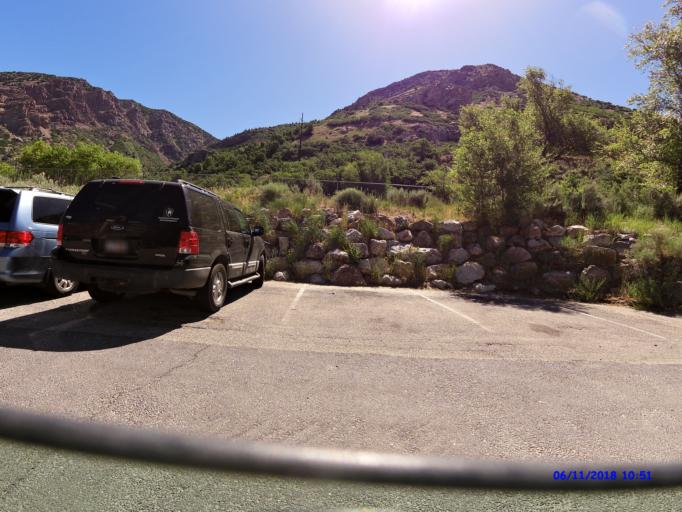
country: US
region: Utah
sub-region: Weber County
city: Ogden
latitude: 41.2108
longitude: -111.9319
